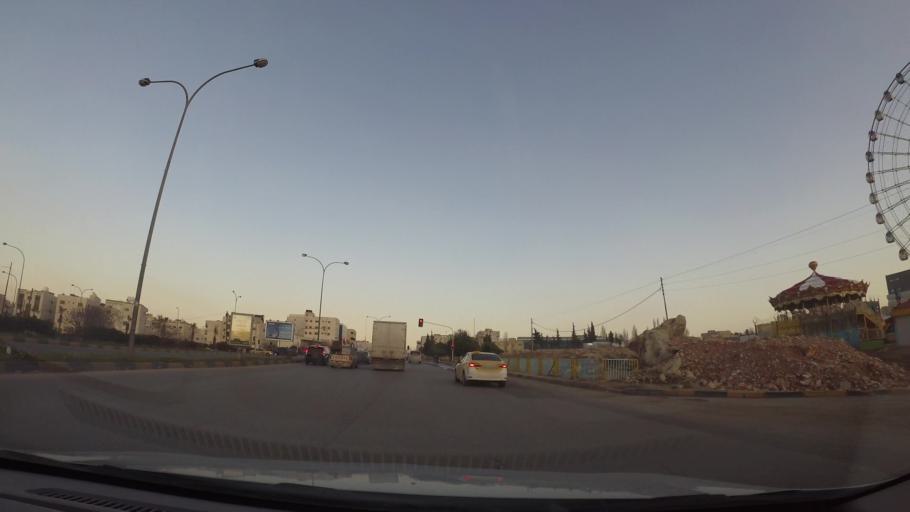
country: JO
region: Amman
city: Al Quwaysimah
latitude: 31.9128
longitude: 35.9186
